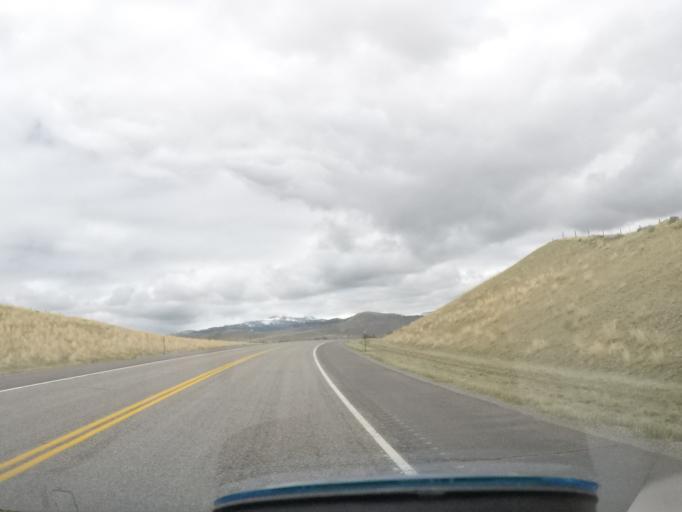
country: US
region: Wyoming
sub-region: Sublette County
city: Pinedale
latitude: 43.5865
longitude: -109.7706
